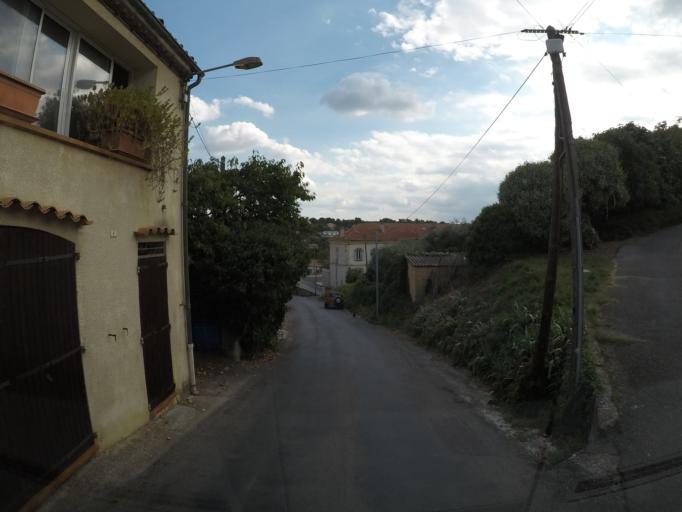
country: FR
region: Provence-Alpes-Cote d'Azur
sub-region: Departement des Alpes-de-Haute-Provence
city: Valensole
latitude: 43.8363
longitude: 5.9824
